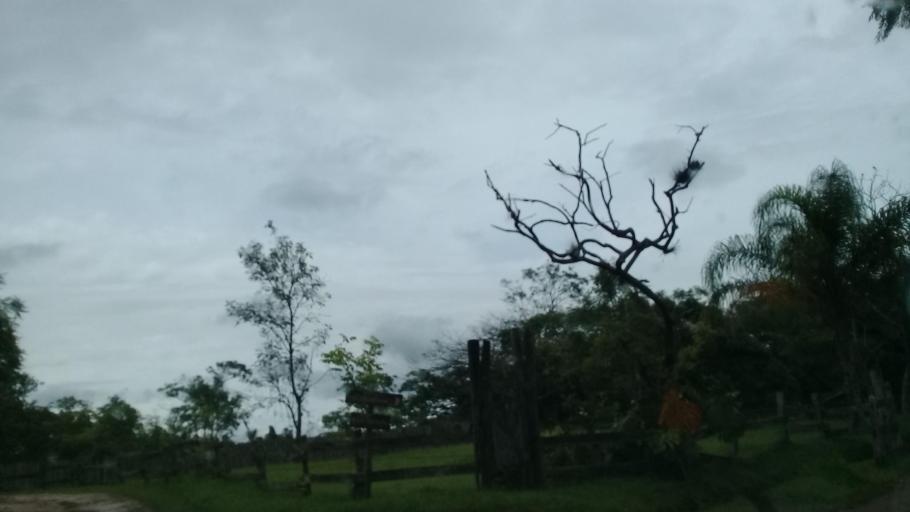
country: MX
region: Veracruz
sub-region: Emiliano Zapata
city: Jacarandas
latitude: 19.5076
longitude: -96.8433
